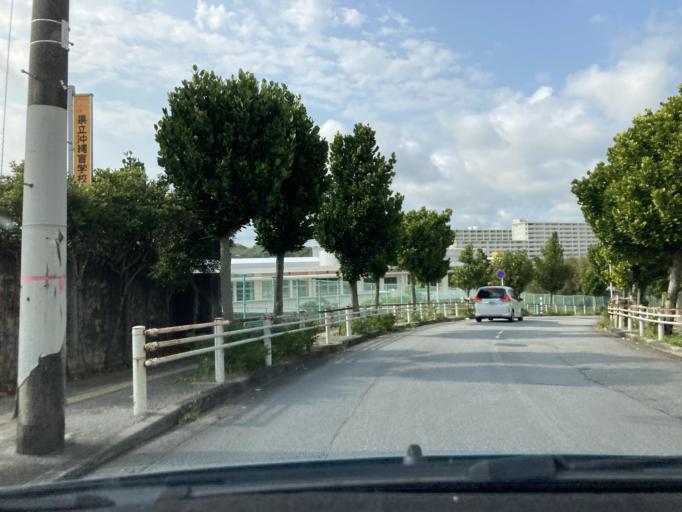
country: JP
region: Okinawa
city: Tomigusuku
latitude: 26.1976
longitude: 127.7211
